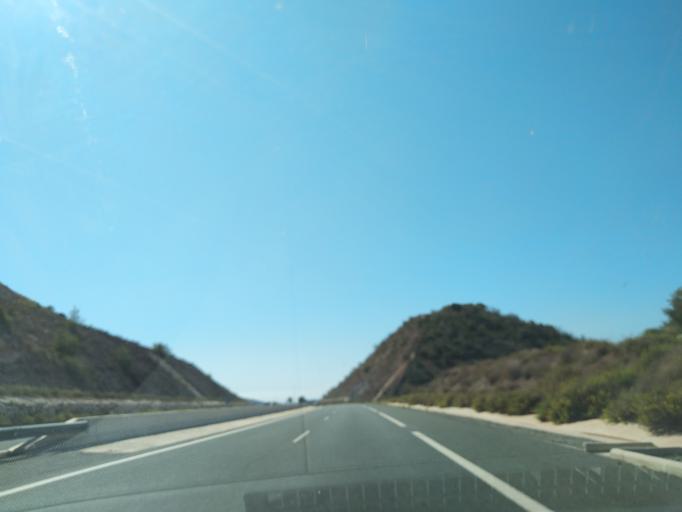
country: ES
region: Andalusia
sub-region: Provincia de Malaga
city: Almogia
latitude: 36.8239
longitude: -4.4702
